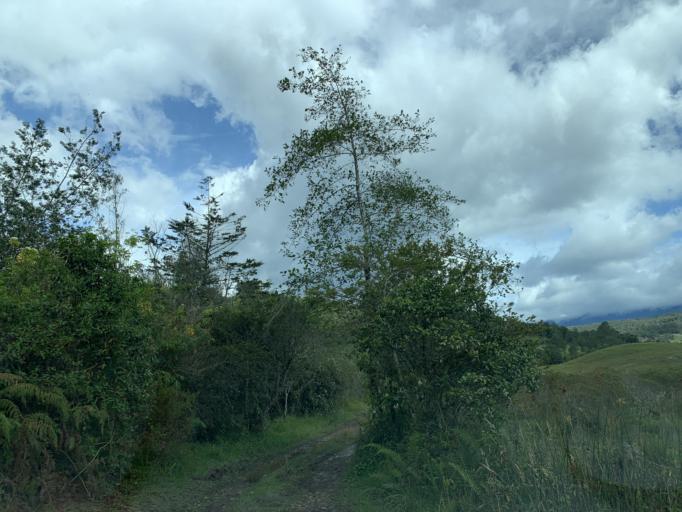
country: CO
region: Boyaca
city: Arcabuco
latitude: 5.7939
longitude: -73.4574
